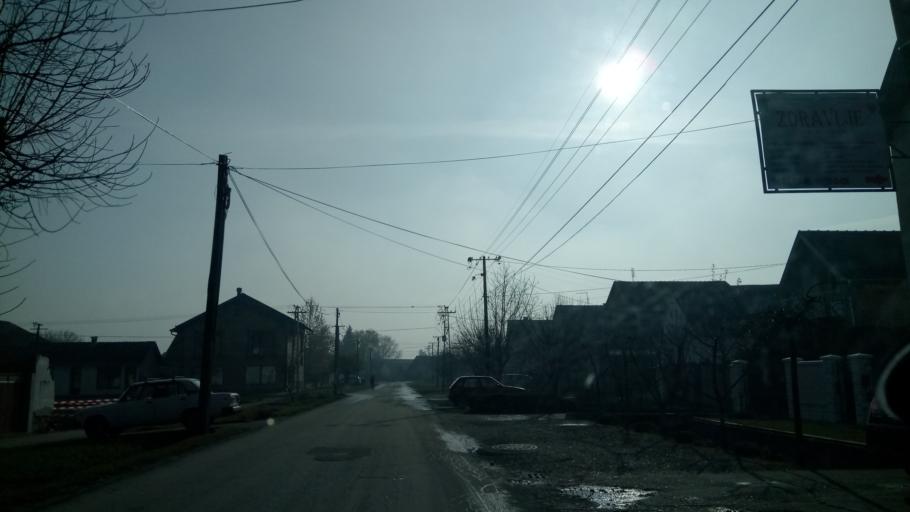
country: RS
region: Autonomna Pokrajina Vojvodina
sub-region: Sremski Okrug
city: Stara Pazova
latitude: 44.9830
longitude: 20.1707
